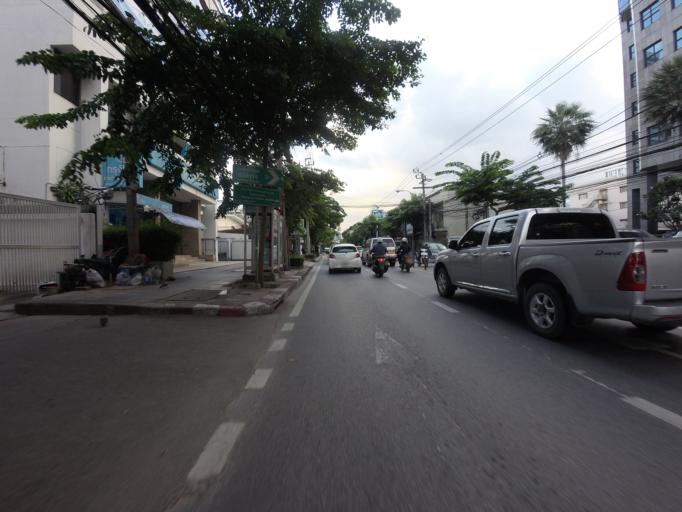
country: TH
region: Bangkok
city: Watthana
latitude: 13.7390
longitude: 100.5892
